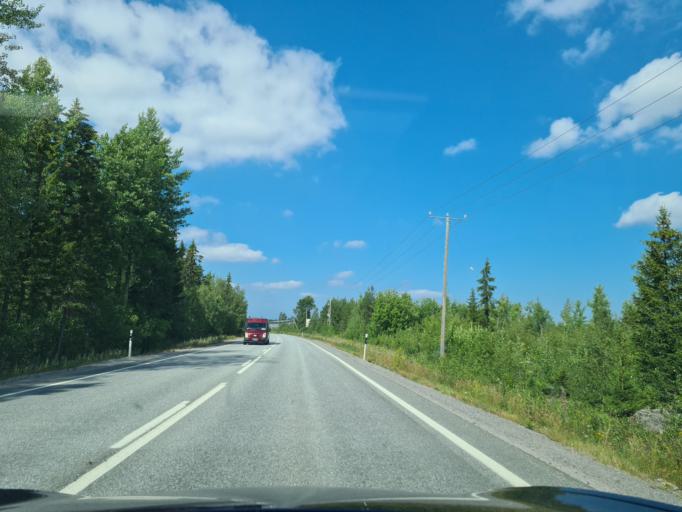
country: FI
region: Ostrobothnia
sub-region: Vaasa
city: Vaasa
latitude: 63.1651
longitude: 21.5899
